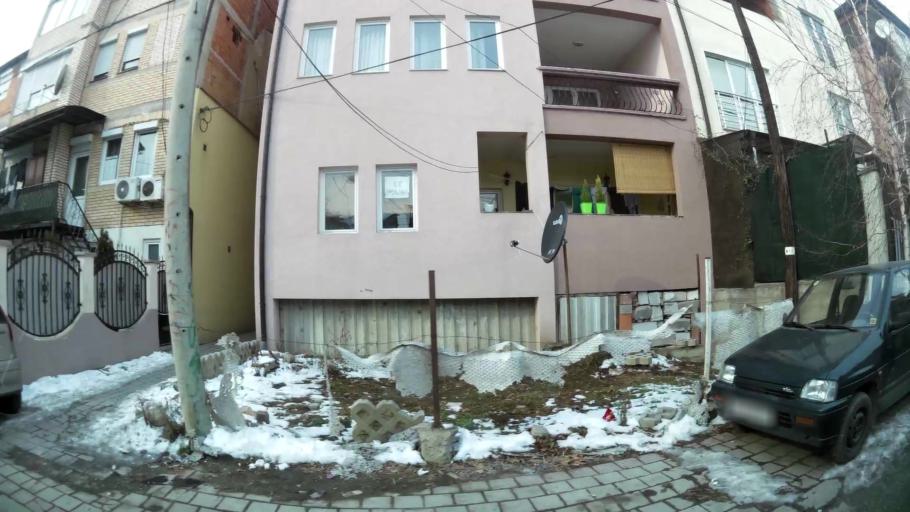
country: MK
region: Cair
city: Cair
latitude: 42.0106
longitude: 21.4426
